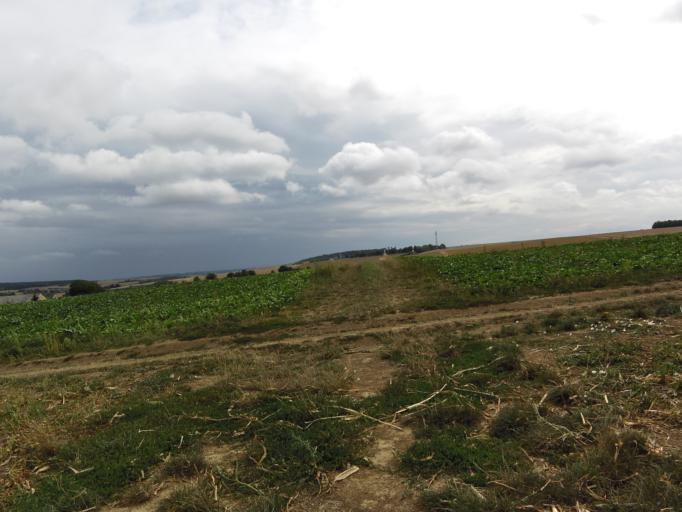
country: DE
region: Bavaria
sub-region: Regierungsbezirk Unterfranken
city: Rimpar
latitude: 49.8545
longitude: 9.9443
